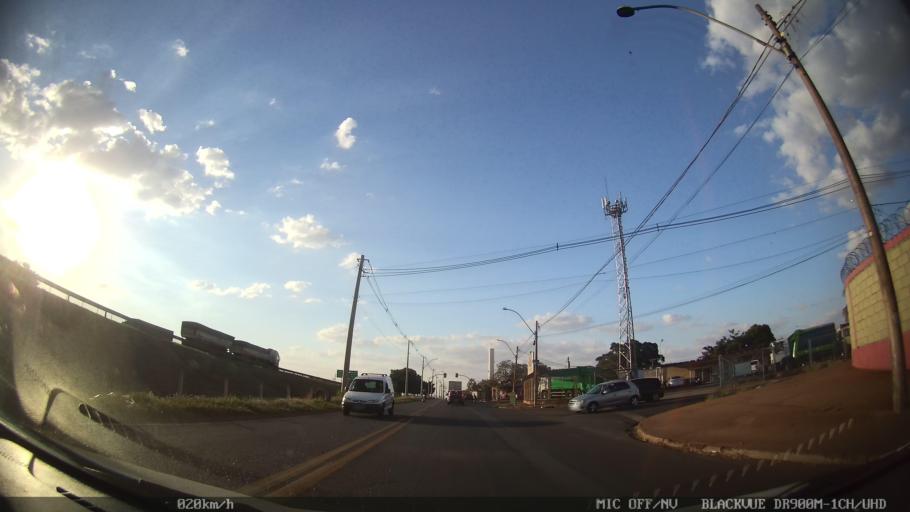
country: BR
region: Sao Paulo
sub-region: Ribeirao Preto
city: Ribeirao Preto
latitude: -21.1857
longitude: -47.7580
